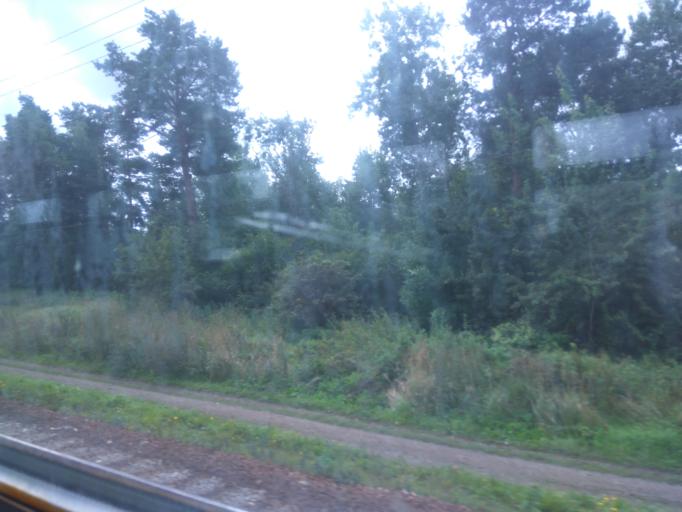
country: RU
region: Moskovskaya
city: Beloozerskiy
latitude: 55.4739
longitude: 38.4234
